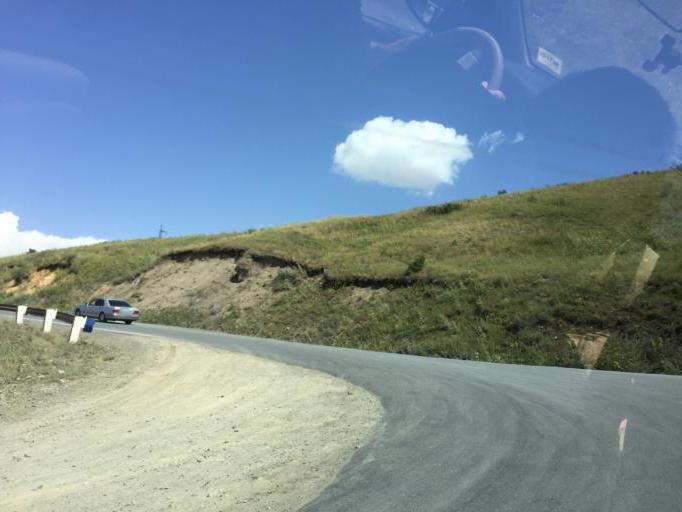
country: AM
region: Vayots' Dzori Marz
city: Jermuk
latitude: 39.6894
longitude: 45.6965
